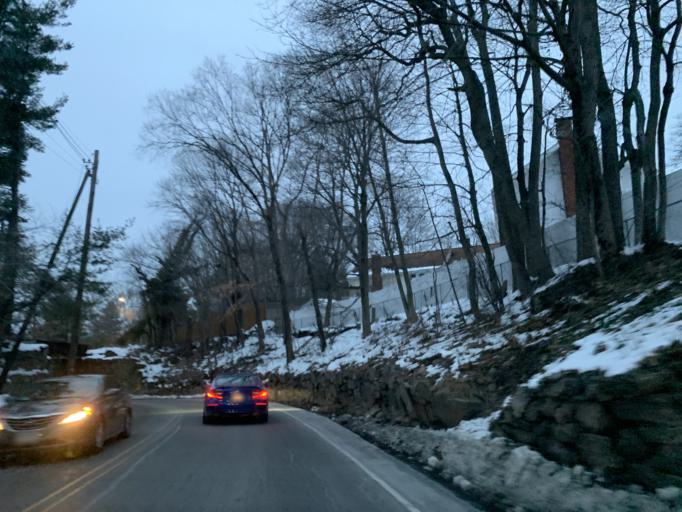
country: US
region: Massachusetts
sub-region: Norfolk County
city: Canton
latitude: 42.1520
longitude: -71.1364
